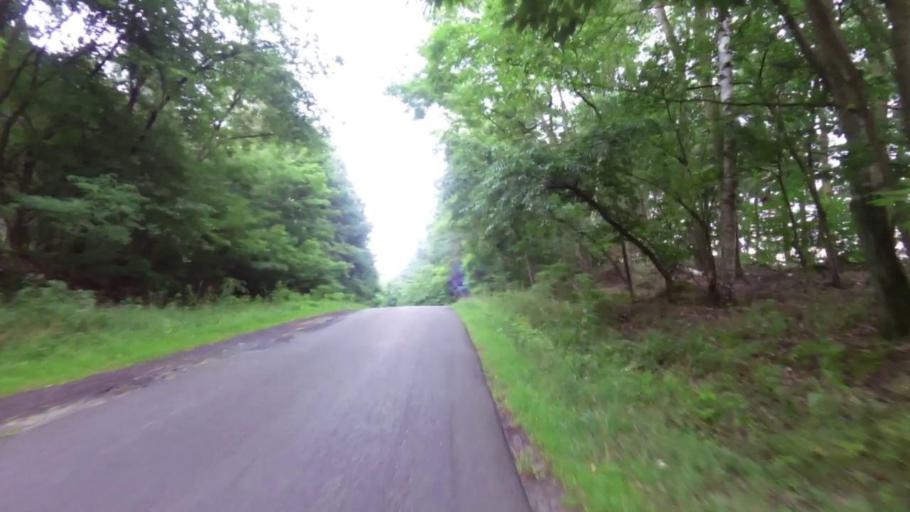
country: PL
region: West Pomeranian Voivodeship
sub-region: Powiat gryfinski
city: Chojna
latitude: 52.9099
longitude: 14.4711
